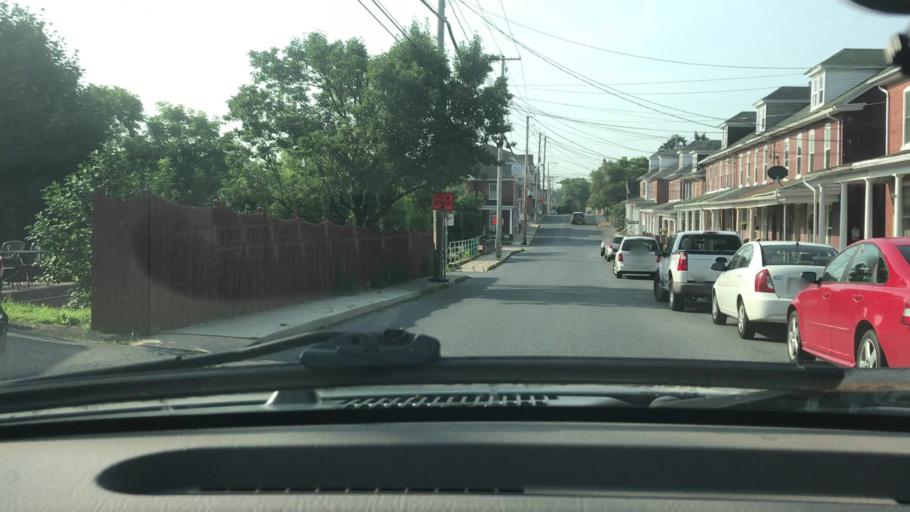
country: US
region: Pennsylvania
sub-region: Lancaster County
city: Elizabethtown
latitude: 40.1523
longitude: -76.6084
